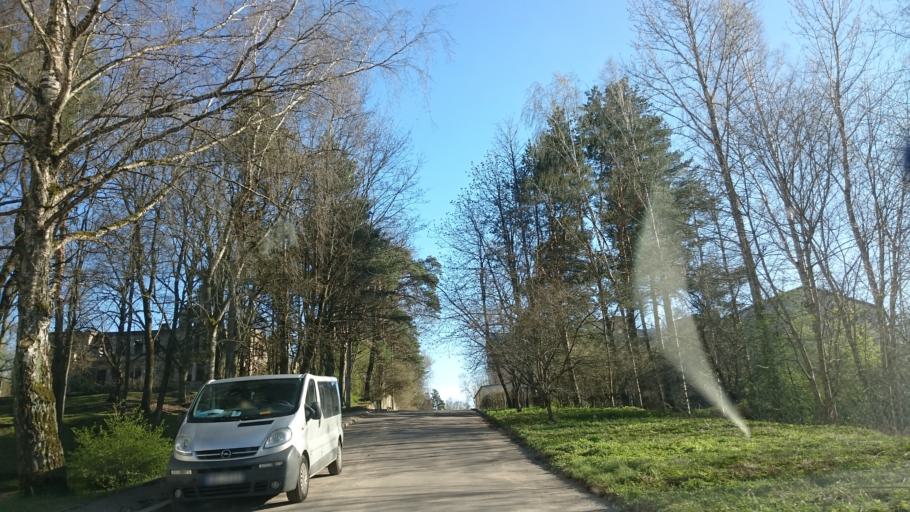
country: LV
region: Riga
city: Bergi
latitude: 56.9950
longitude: 24.2313
